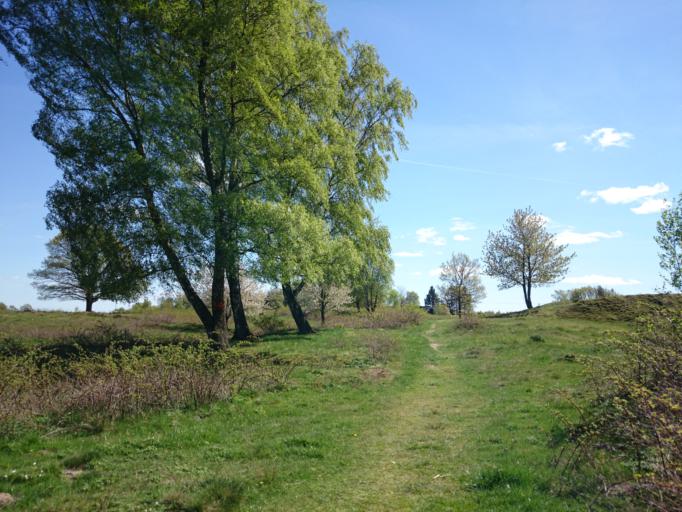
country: SE
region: Skane
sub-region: Lunds Kommun
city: Genarp
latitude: 55.6598
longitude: 13.4048
